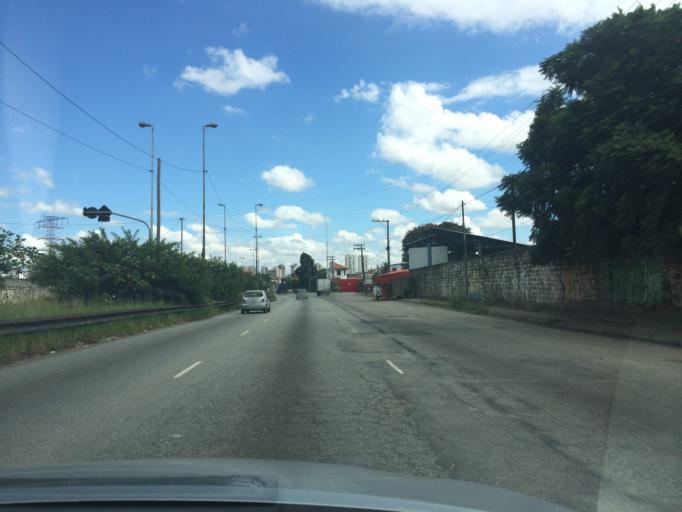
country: BR
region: Sao Paulo
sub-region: Guarulhos
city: Guarulhos
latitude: -23.5142
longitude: -46.5609
